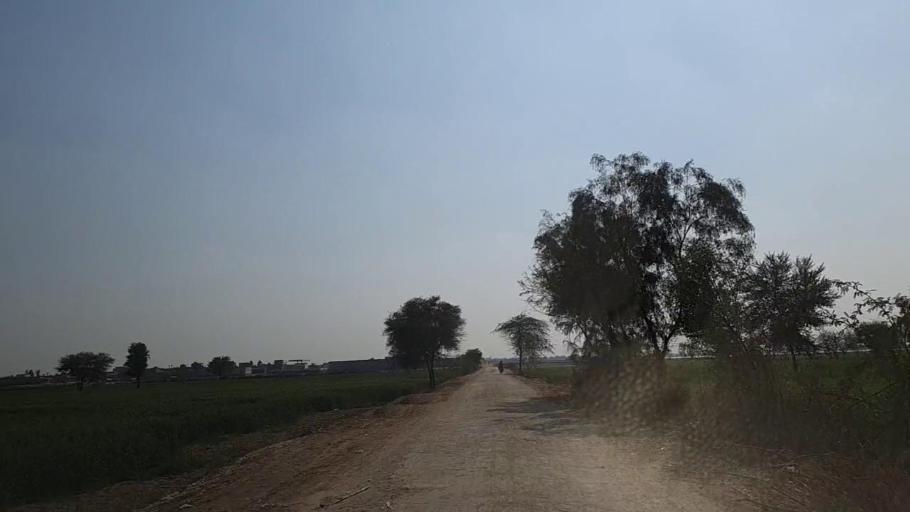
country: PK
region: Sindh
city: Daur
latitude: 26.4668
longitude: 68.2505
